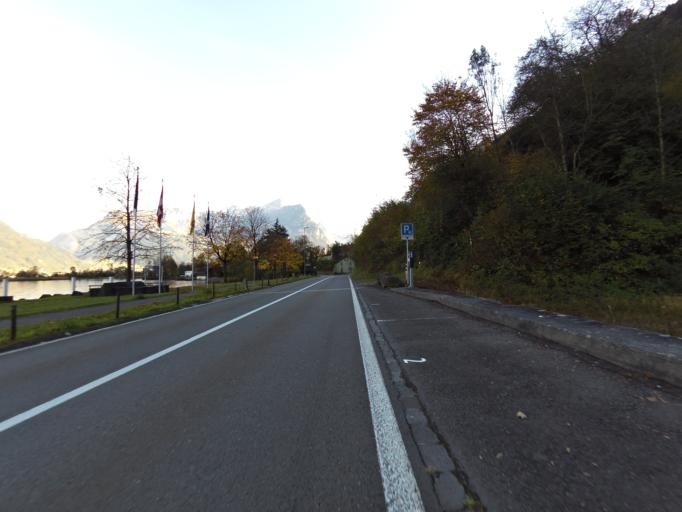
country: CH
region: Uri
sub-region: Uri
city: Seedorf
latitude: 46.8903
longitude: 8.5980
